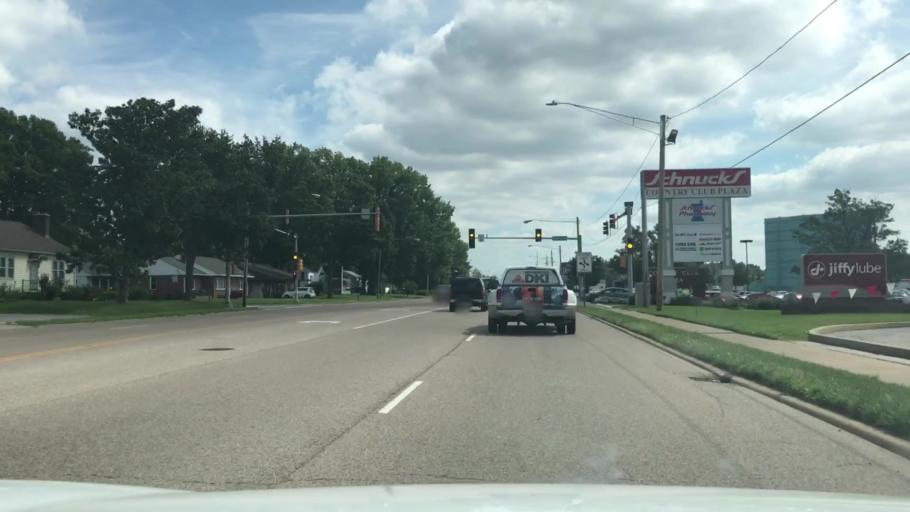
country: US
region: Illinois
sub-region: Saint Clair County
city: Swansea
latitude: 38.5416
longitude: -90.0358
